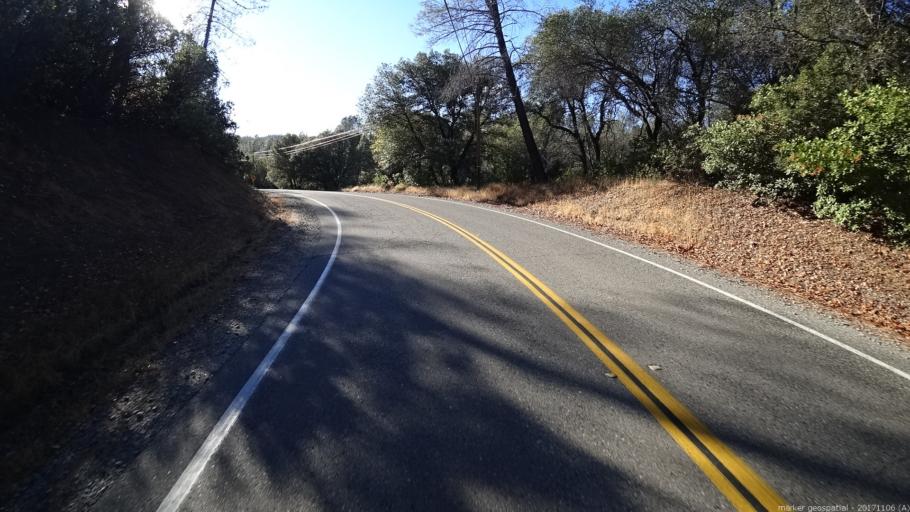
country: US
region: California
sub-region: Shasta County
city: Shasta
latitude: 40.5899
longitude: -122.4820
